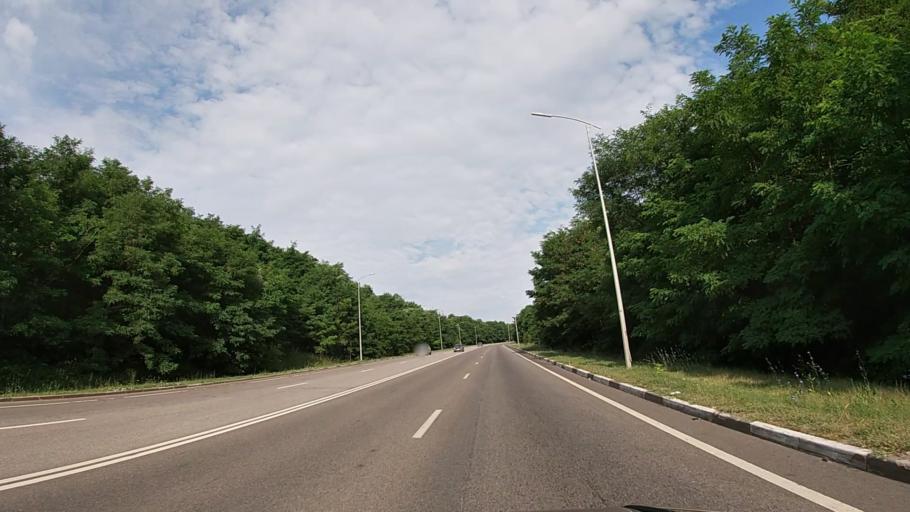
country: RU
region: Belgorod
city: Severnyy
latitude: 50.6357
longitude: 36.4557
